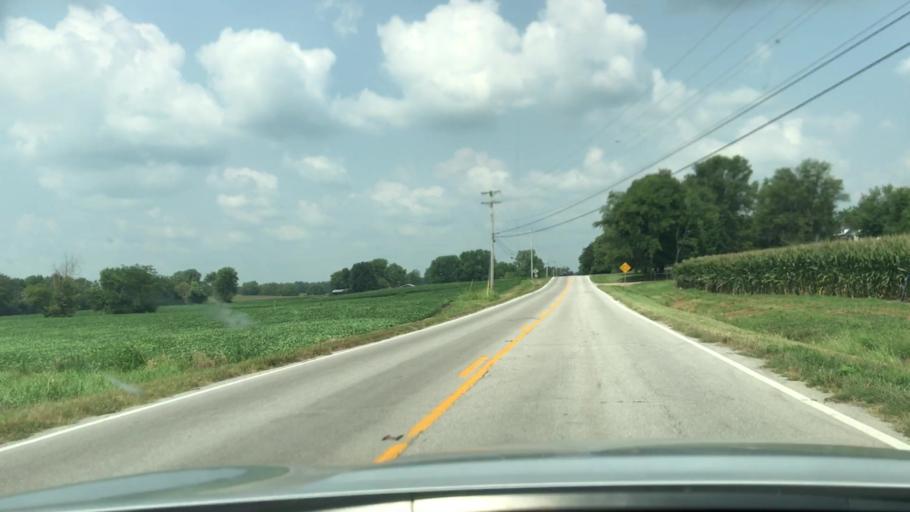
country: US
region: Kentucky
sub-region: Todd County
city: Elkton
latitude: 36.8050
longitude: -87.1253
